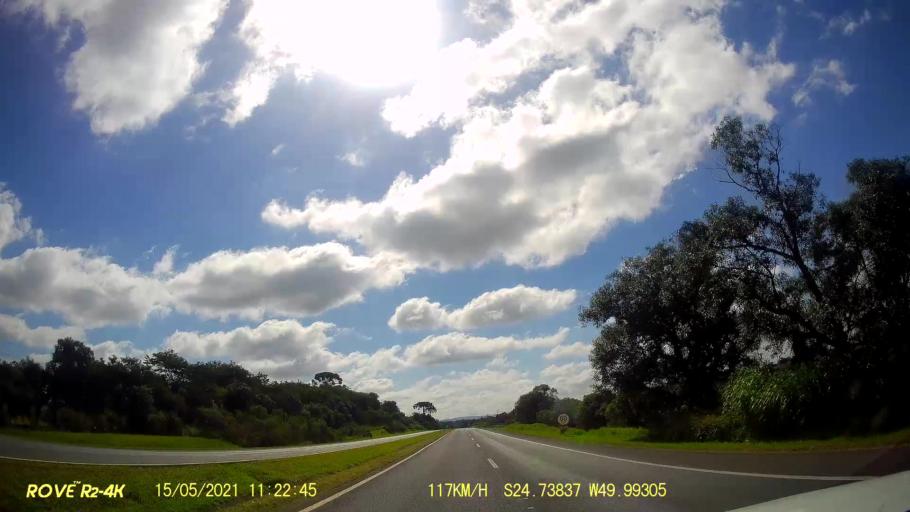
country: BR
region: Parana
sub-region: Castro
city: Castro
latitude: -24.7401
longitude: -49.9942
